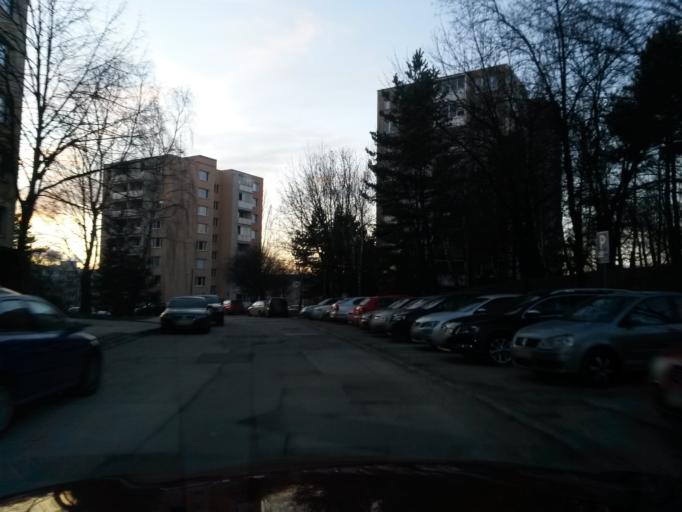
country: SK
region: Kosicky
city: Kosice
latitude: 48.7385
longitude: 21.2881
